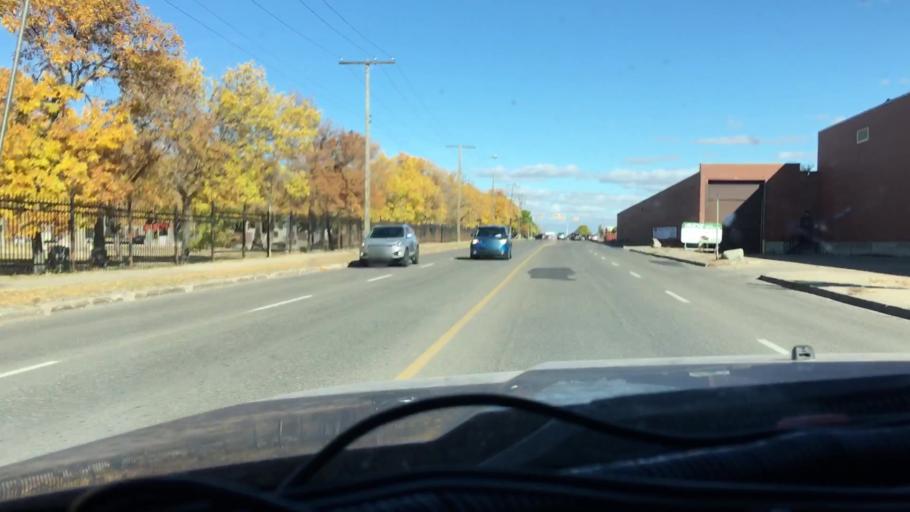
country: CA
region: Saskatchewan
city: Regina
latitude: 50.4629
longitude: -104.6103
